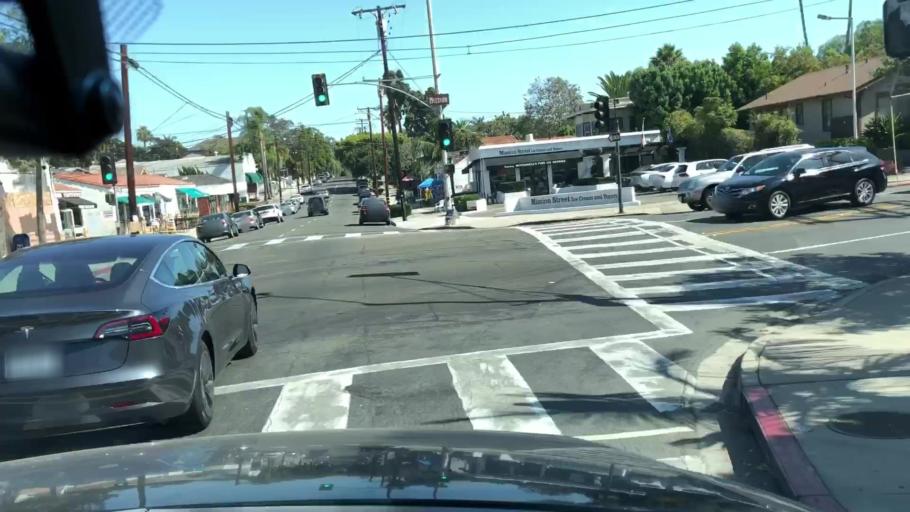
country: US
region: California
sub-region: Santa Barbara County
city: Santa Barbara
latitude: 34.4288
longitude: -119.7171
